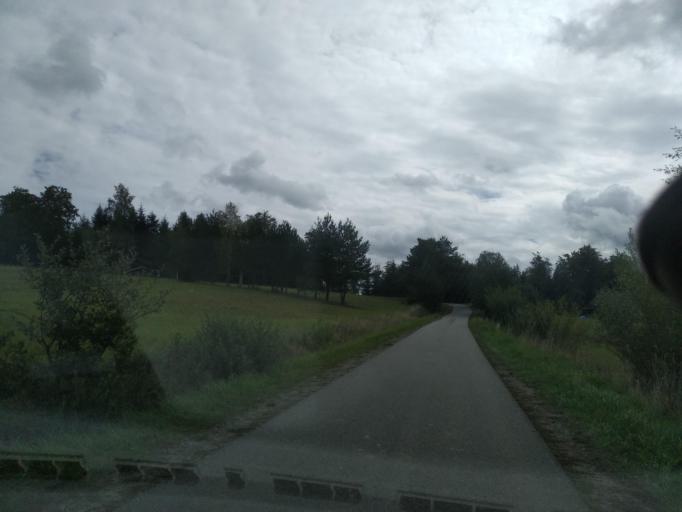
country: PL
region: Lesser Poland Voivodeship
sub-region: Powiat gorlicki
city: Uscie Gorlickie
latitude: 49.5339
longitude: 21.1743
